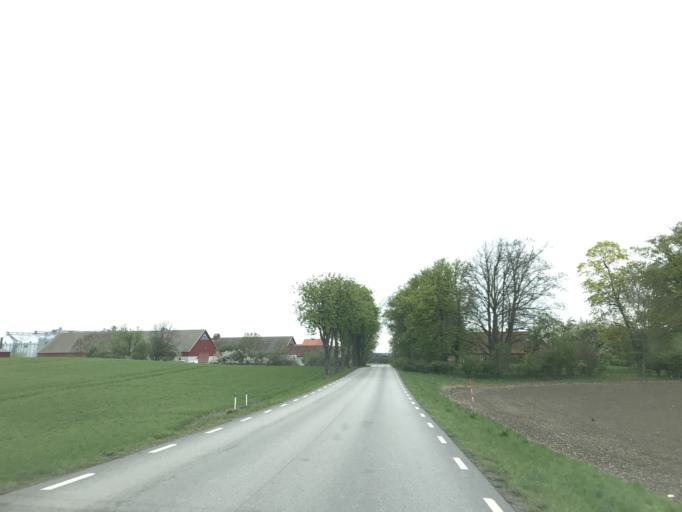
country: SE
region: Skane
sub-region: Trelleborgs Kommun
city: Anderslov
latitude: 55.4885
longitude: 13.3394
